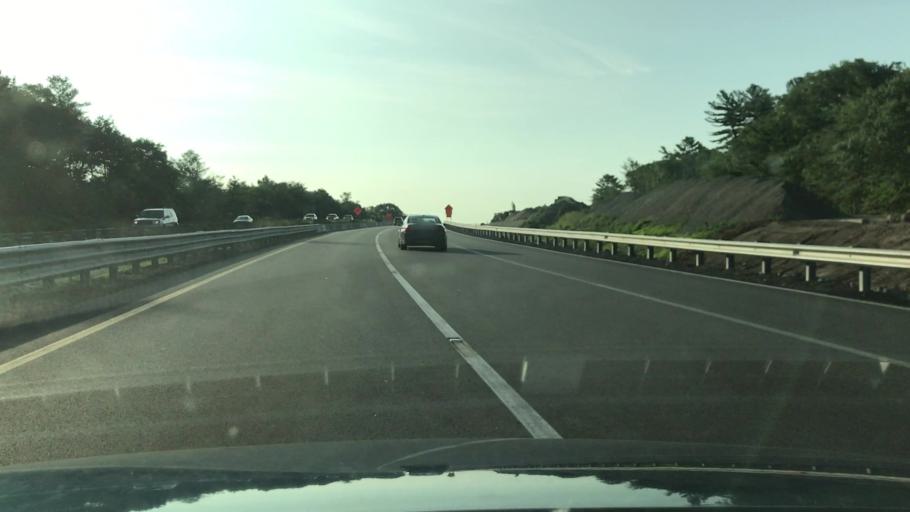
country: US
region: Massachusetts
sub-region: Plymouth County
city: Rockland
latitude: 42.1560
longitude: -70.8585
